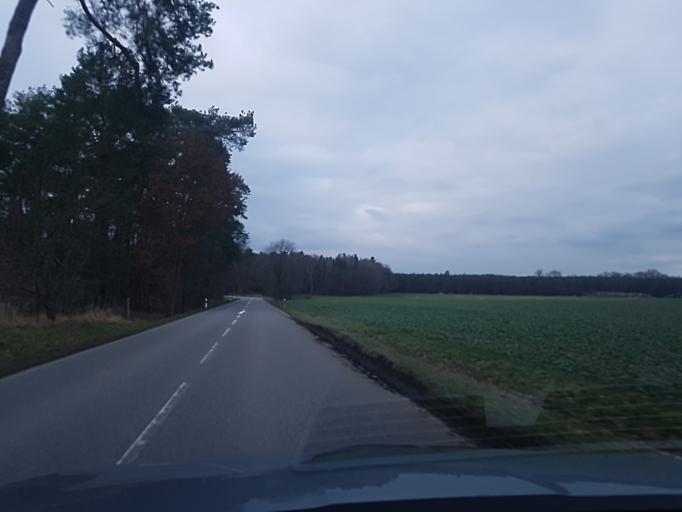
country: DE
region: Brandenburg
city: Finsterwalde
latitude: 51.6738
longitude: 13.6908
